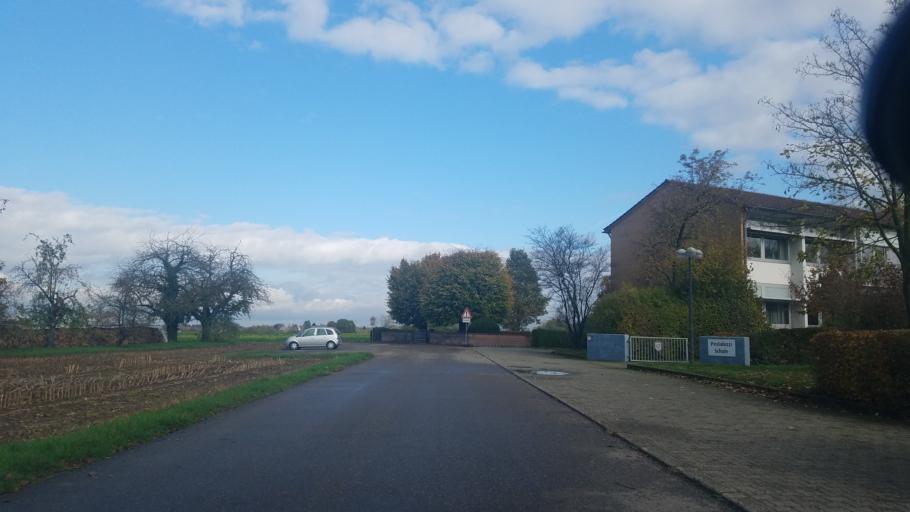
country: DE
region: Baden-Wuerttemberg
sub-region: Karlsruhe Region
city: Lichtenau
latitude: 48.6828
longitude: 7.9828
